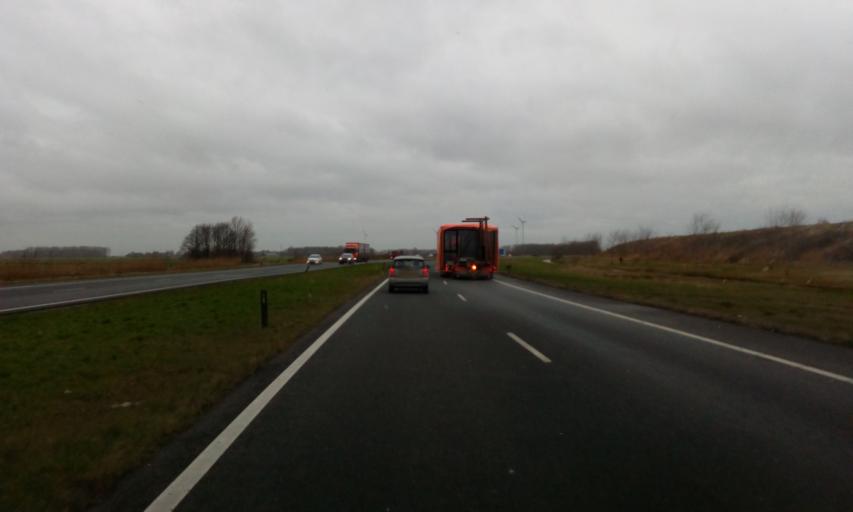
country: NL
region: South Holland
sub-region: Gemeente Alphen aan den Rijn
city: Alphen aan den Rijn
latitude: 52.1121
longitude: 4.6416
